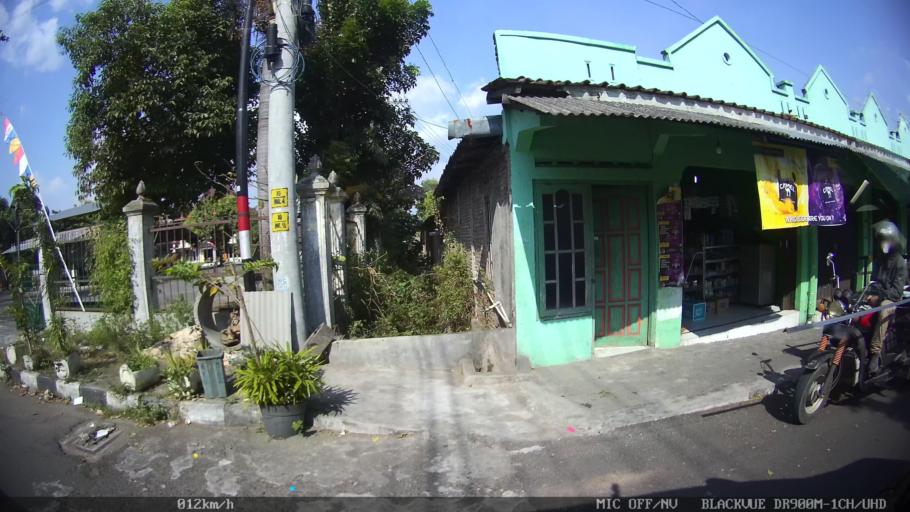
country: ID
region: Daerah Istimewa Yogyakarta
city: Sewon
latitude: -7.8362
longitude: 110.3934
